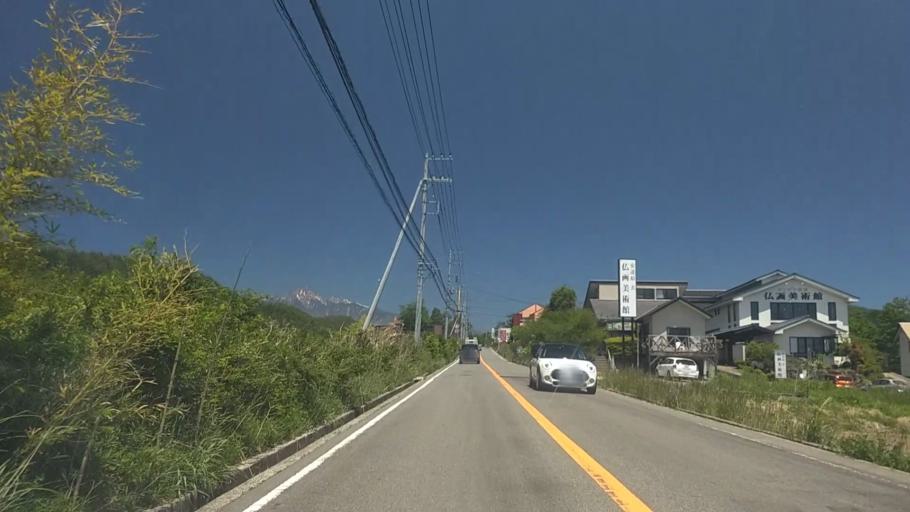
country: JP
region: Yamanashi
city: Nirasaki
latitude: 35.8460
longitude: 138.4329
